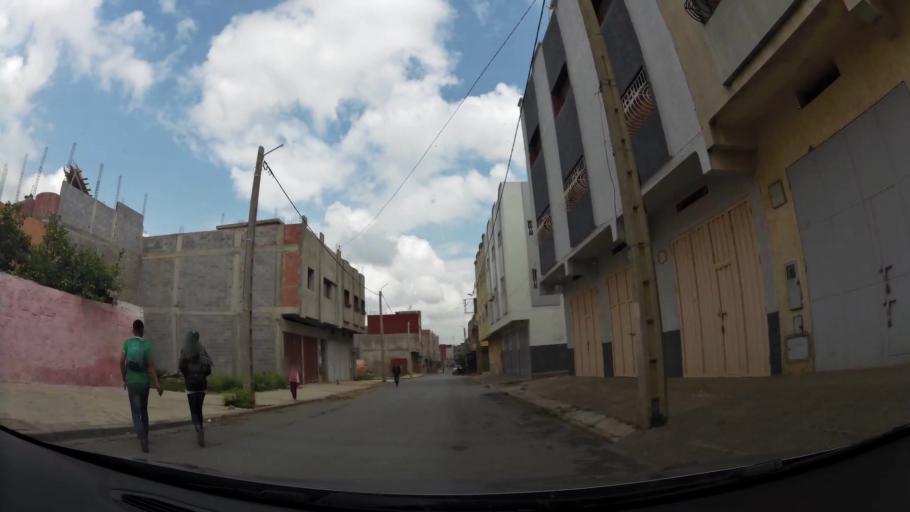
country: MA
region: Rabat-Sale-Zemmour-Zaer
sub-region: Khemisset
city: Tiflet
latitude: 33.8891
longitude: -6.3250
